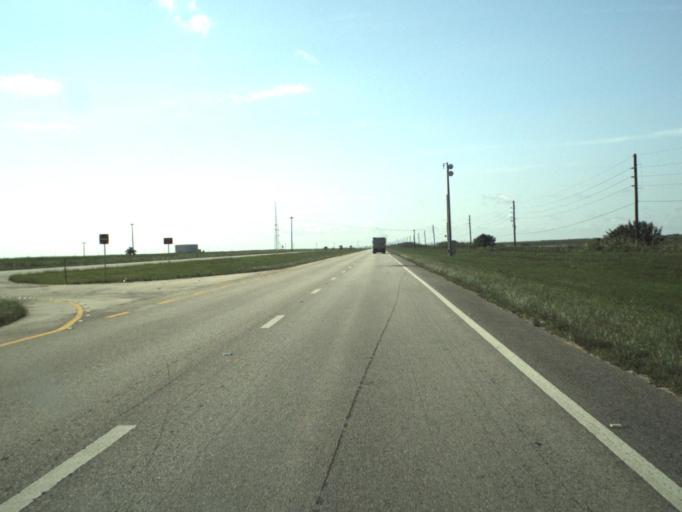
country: US
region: Florida
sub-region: Palm Beach County
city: Belle Glade Camp
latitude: 26.4464
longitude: -80.6243
